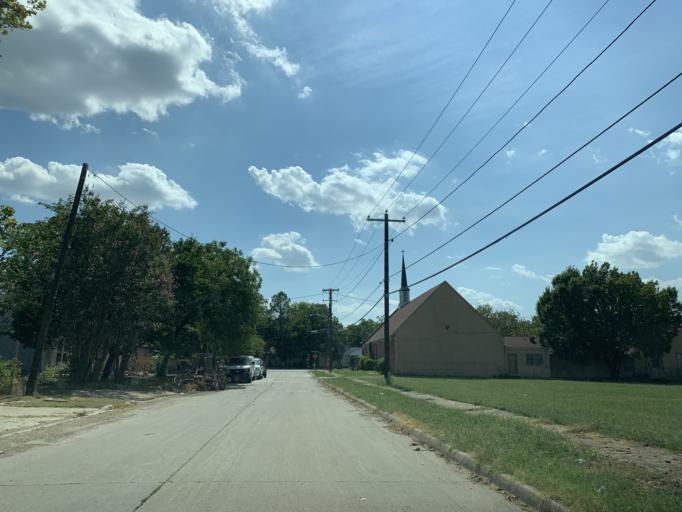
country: US
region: Texas
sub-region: Dallas County
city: Hutchins
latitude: 32.7058
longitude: -96.7719
